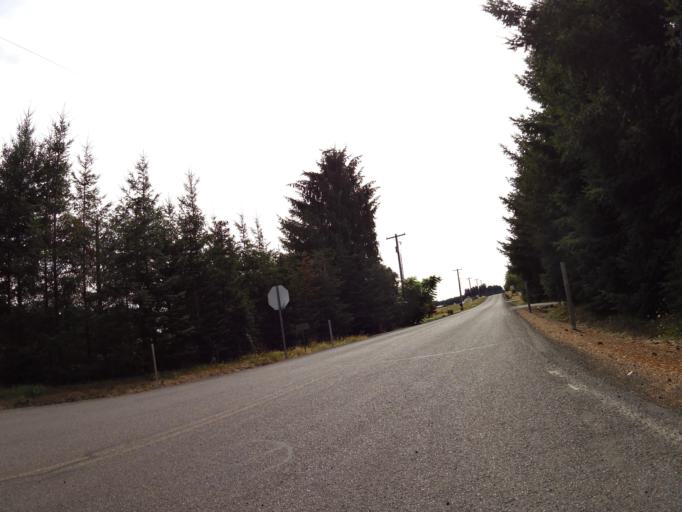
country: US
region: Washington
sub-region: Lewis County
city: Napavine
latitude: 46.5434
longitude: -122.9496
